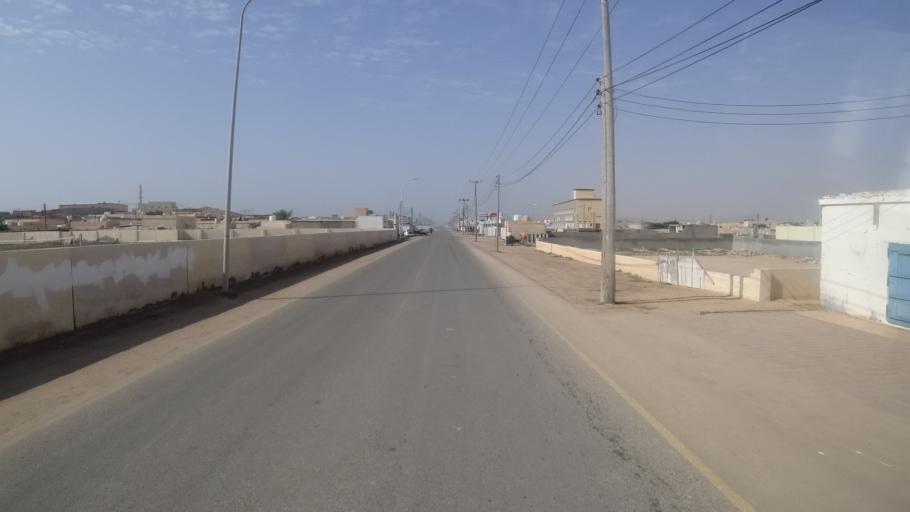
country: OM
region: Ash Sharqiyah
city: Sur
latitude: 22.1814
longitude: 59.7629
